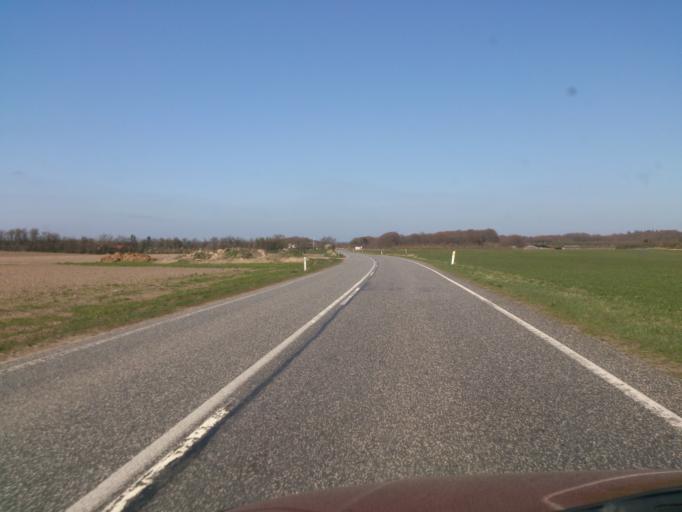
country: DK
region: Central Jutland
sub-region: Viborg Kommune
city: Bjerringbro
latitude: 56.4307
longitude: 9.6780
